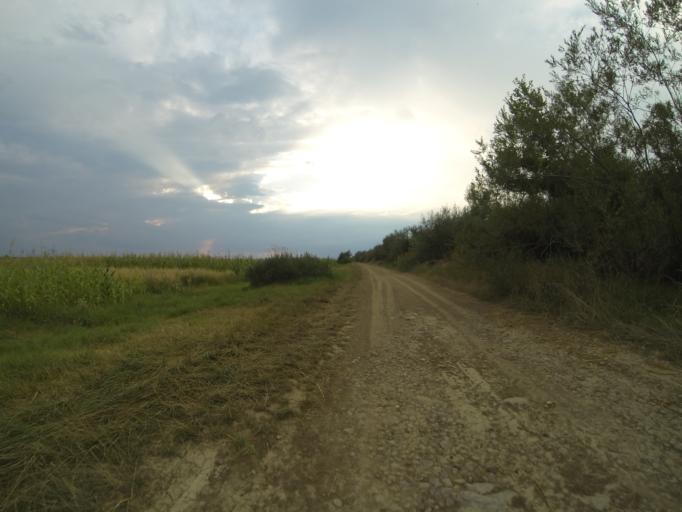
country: RO
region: Brasov
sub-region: Comuna Sinca Veche
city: Sinca Veche
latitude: 45.7717
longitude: 25.1713
